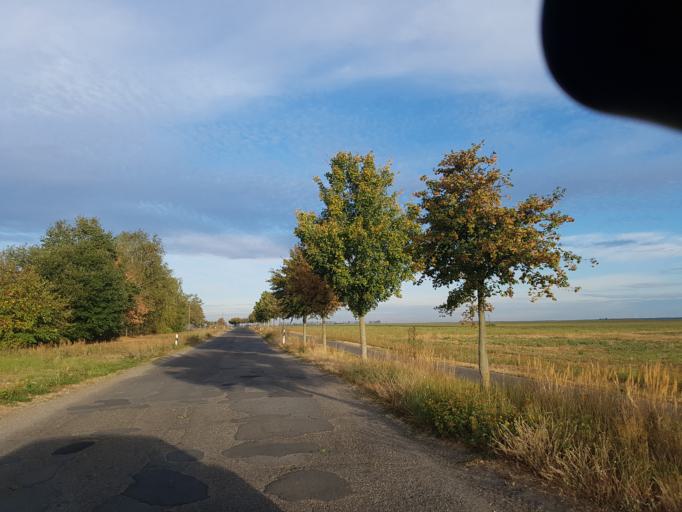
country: DE
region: Brandenburg
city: Dahme
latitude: 51.8582
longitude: 13.4109
